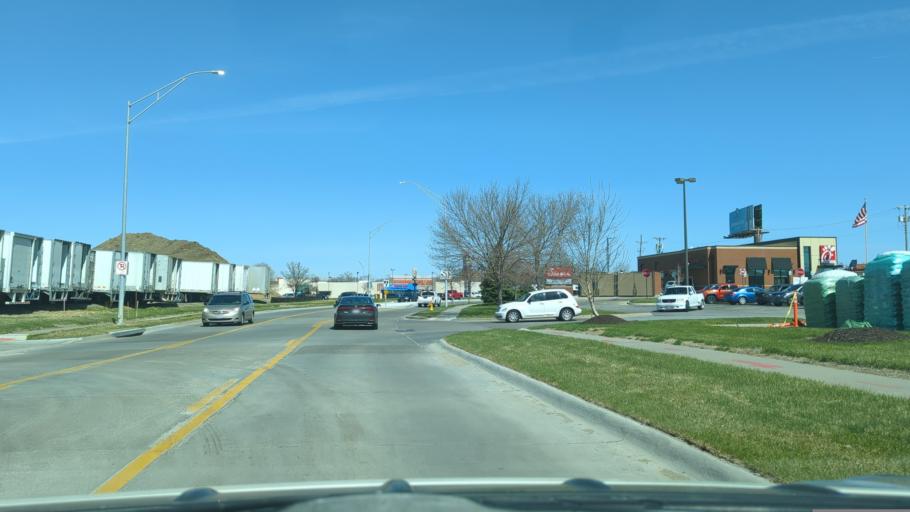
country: US
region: Nebraska
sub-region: Douglas County
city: Ralston
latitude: 41.2580
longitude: -96.0311
